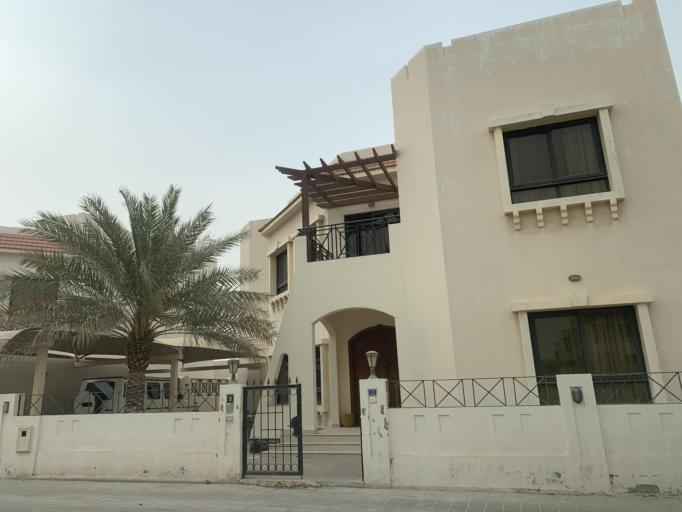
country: BH
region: Central Governorate
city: Madinat Hamad
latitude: 26.1401
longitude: 50.5181
